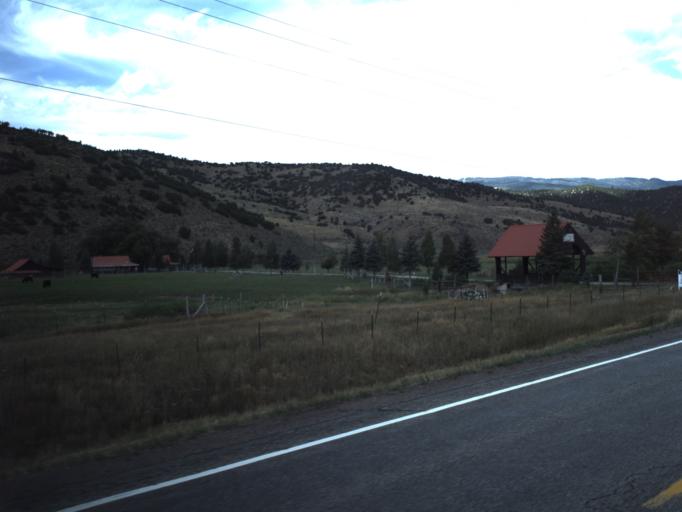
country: US
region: Utah
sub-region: Utah County
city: Woodland Hills
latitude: 39.8621
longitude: -111.5283
